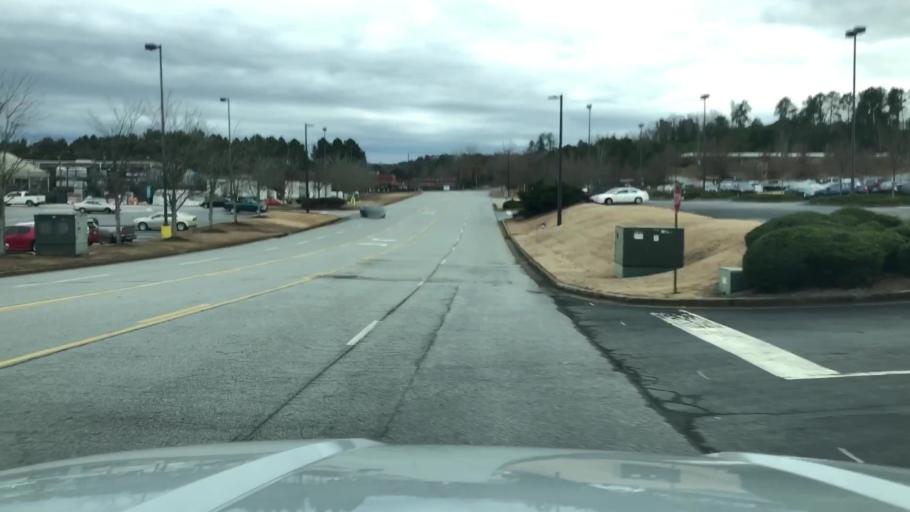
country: US
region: Georgia
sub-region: Cherokee County
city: Woodstock
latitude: 34.0829
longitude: -84.5411
